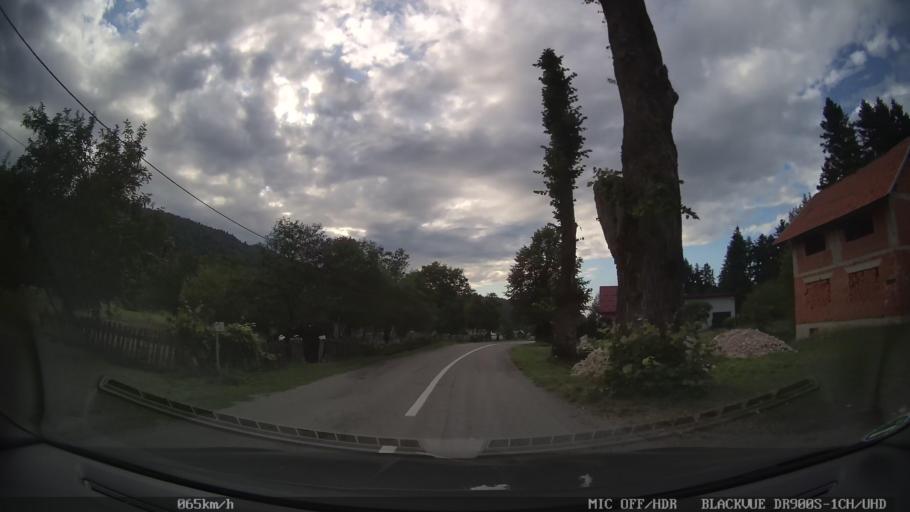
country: HR
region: Licko-Senjska
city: Jezerce
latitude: 44.9481
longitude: 15.5361
